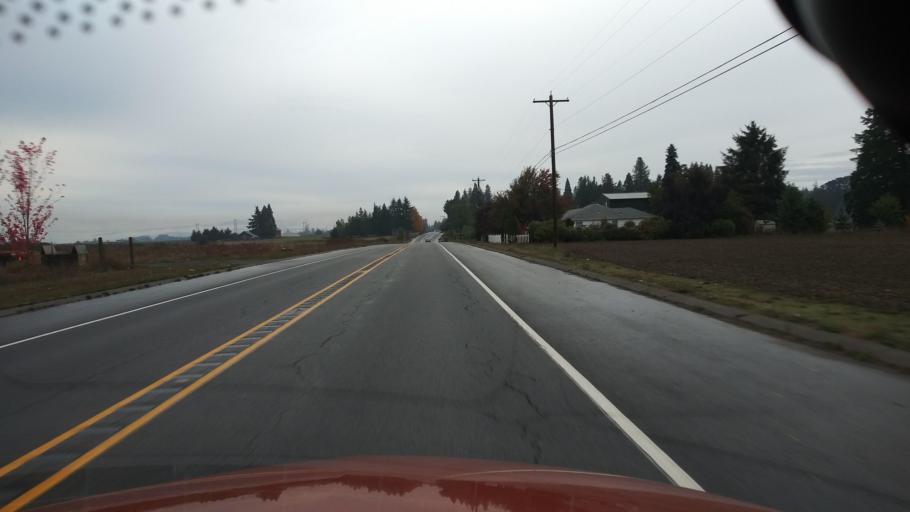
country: US
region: Oregon
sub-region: Washington County
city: Cornelius
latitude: 45.5356
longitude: -123.0598
